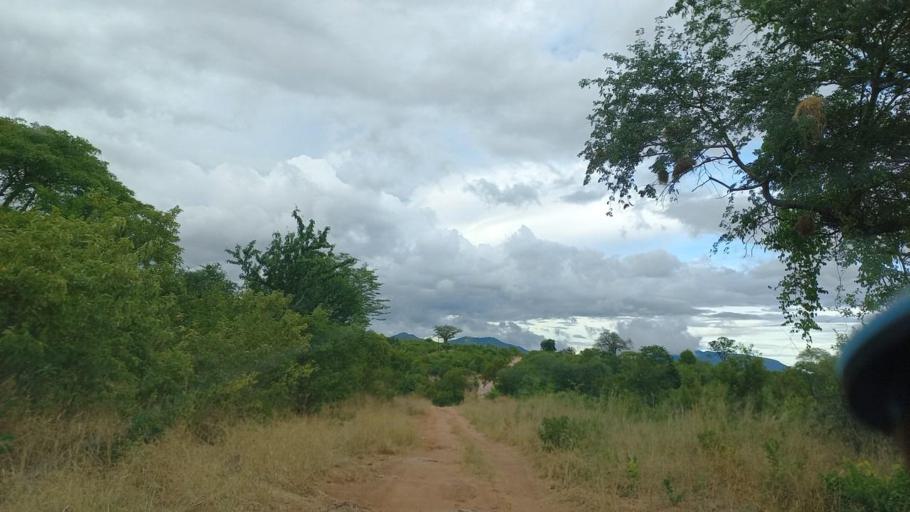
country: ZM
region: Lusaka
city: Luangwa
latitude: -15.5642
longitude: 30.3424
